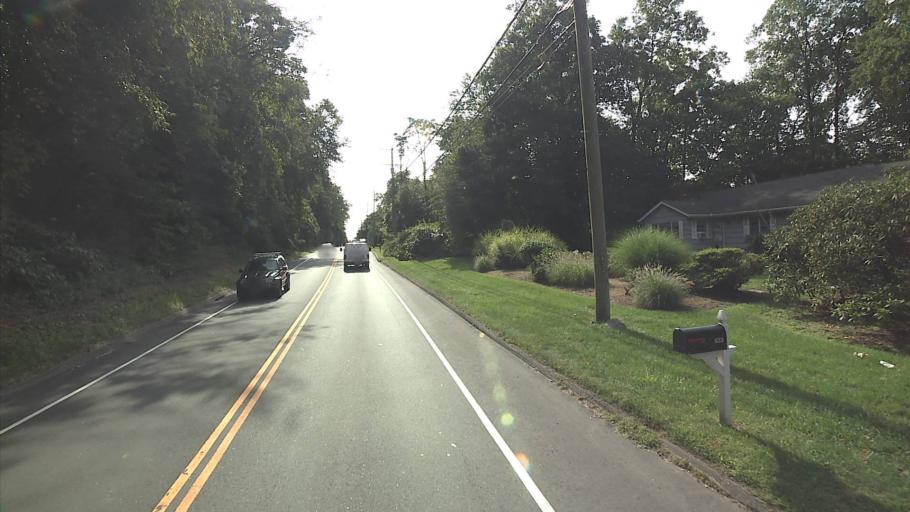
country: US
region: Connecticut
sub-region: Fairfield County
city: New Canaan
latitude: 41.1425
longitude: -73.4774
